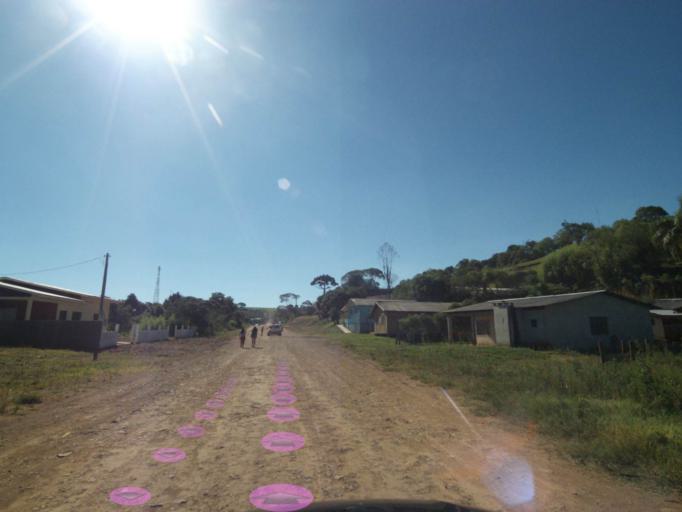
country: BR
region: Parana
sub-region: Coronel Vivida
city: Coronel Vivida
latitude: -26.1423
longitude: -52.3828
